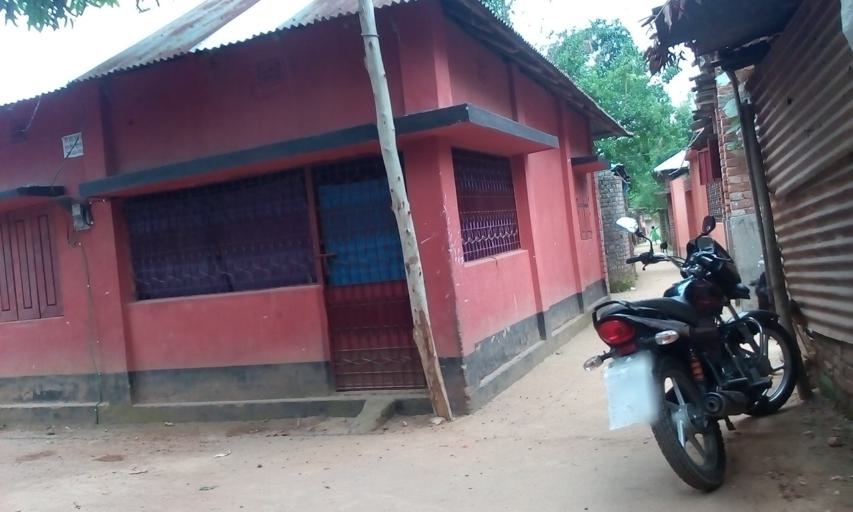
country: IN
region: West Bengal
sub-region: Dakshin Dinajpur
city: Balurghat
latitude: 25.3831
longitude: 88.9954
